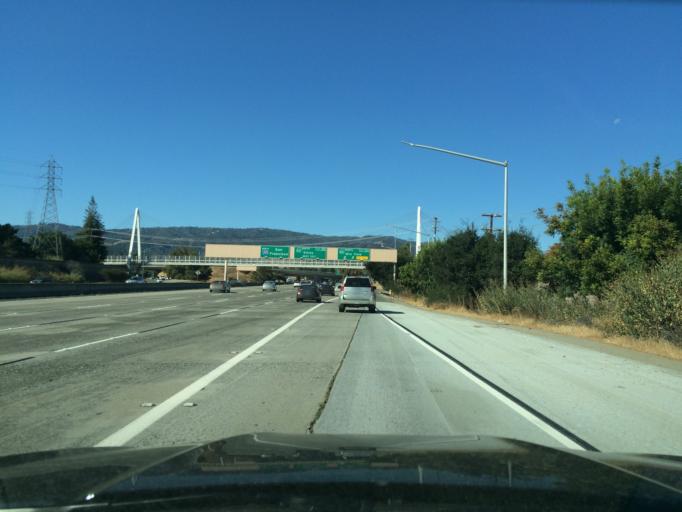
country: US
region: California
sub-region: Santa Clara County
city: Cupertino
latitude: 37.3342
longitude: -122.0484
